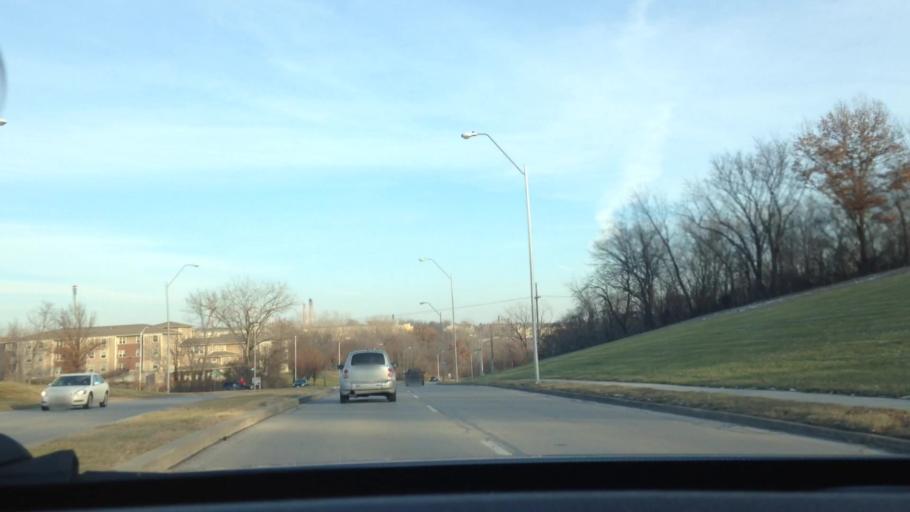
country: US
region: Missouri
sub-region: Clay County
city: Claycomo
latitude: 39.1703
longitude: -94.5048
